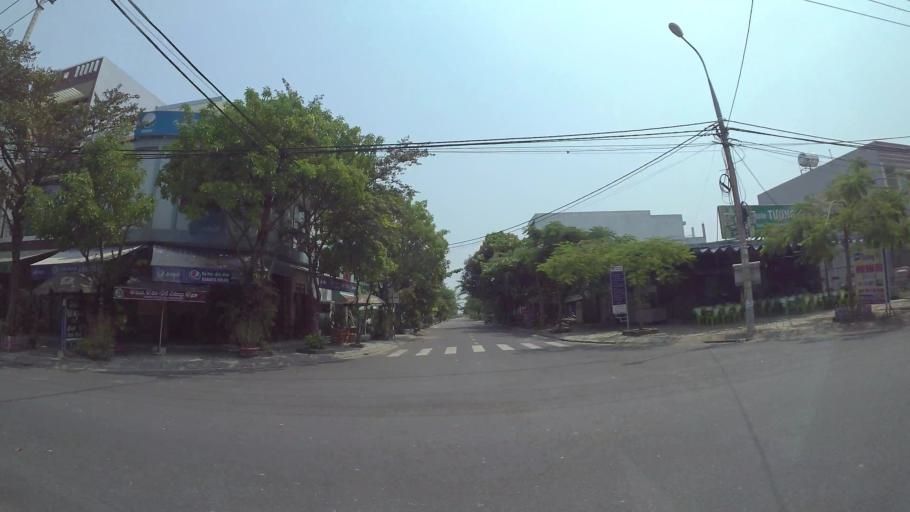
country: VN
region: Da Nang
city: Cam Le
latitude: 15.9953
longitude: 108.2134
